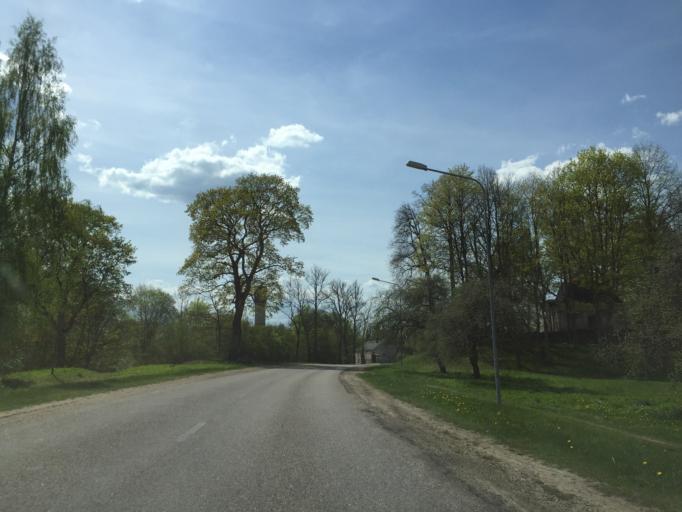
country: LV
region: Limbazu Rajons
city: Limbazi
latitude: 57.3487
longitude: 24.6635
